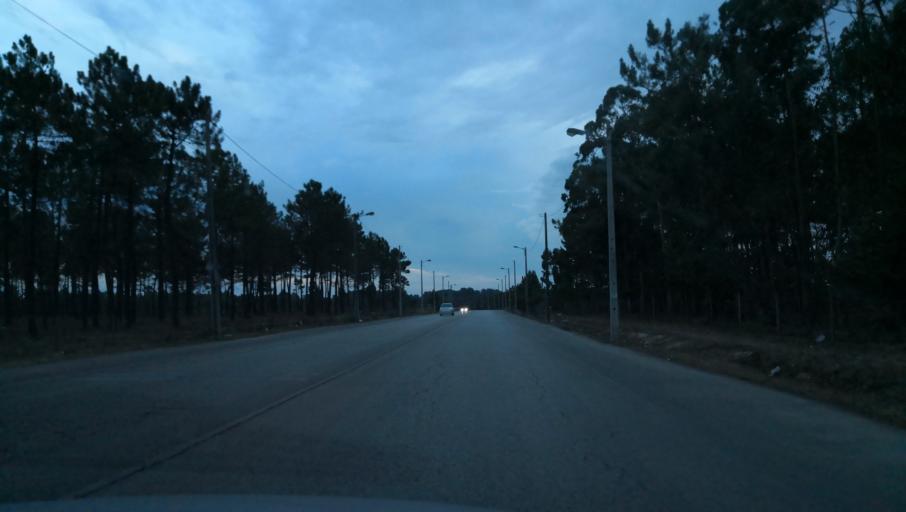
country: PT
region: Setubal
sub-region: Almada
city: Charneca
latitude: 38.5994
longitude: -9.1611
